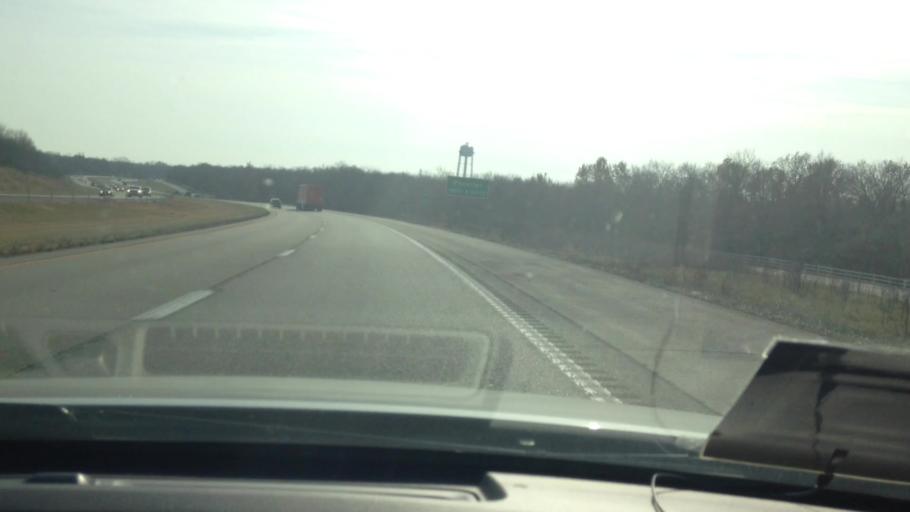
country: US
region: Missouri
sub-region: Cass County
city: Raymore
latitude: 38.7635
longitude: -94.4899
